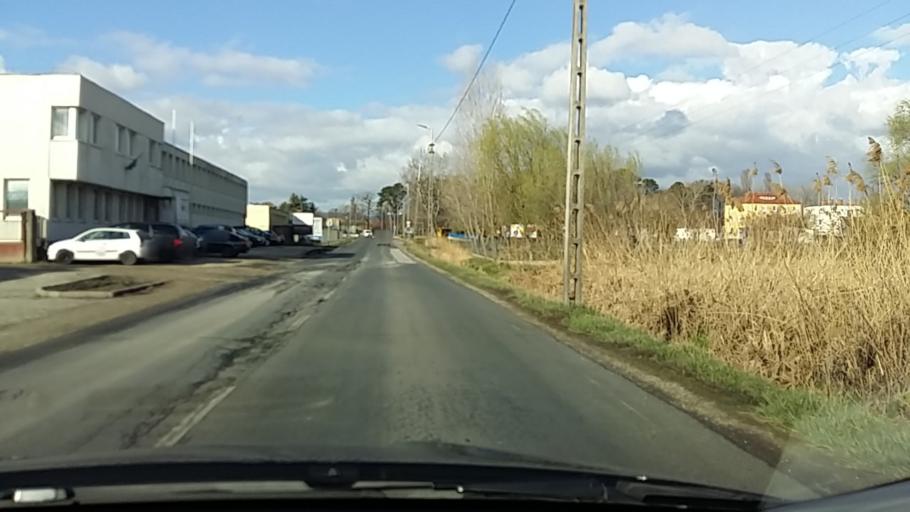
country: HU
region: Veszprem
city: Tapolca
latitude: 46.8780
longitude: 17.4338
